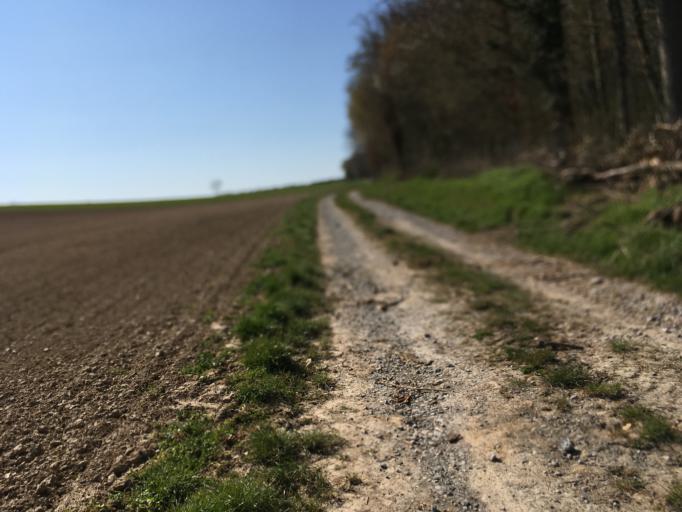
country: DE
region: Baden-Wuerttemberg
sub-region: Regierungsbezirk Stuttgart
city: Bad Rappenau
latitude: 49.1999
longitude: 9.1167
